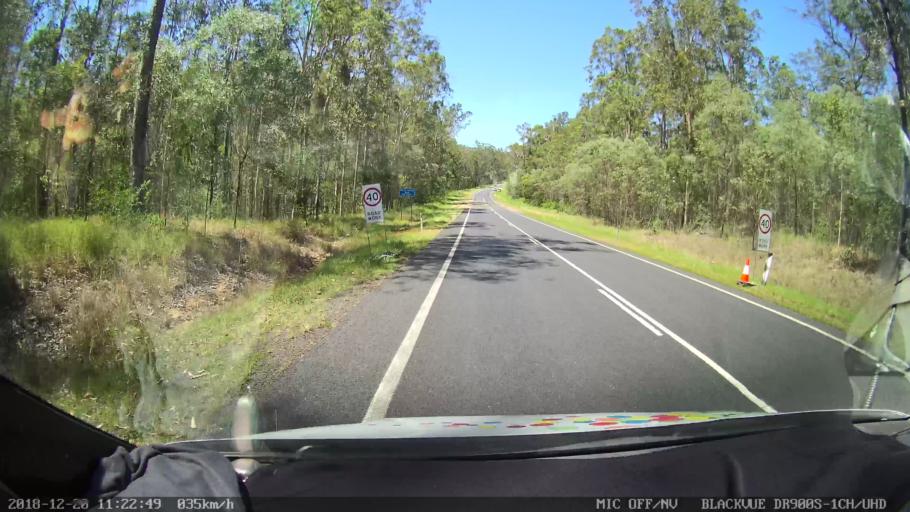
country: AU
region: New South Wales
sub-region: Richmond Valley
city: Casino
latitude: -29.0622
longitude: 153.0049
